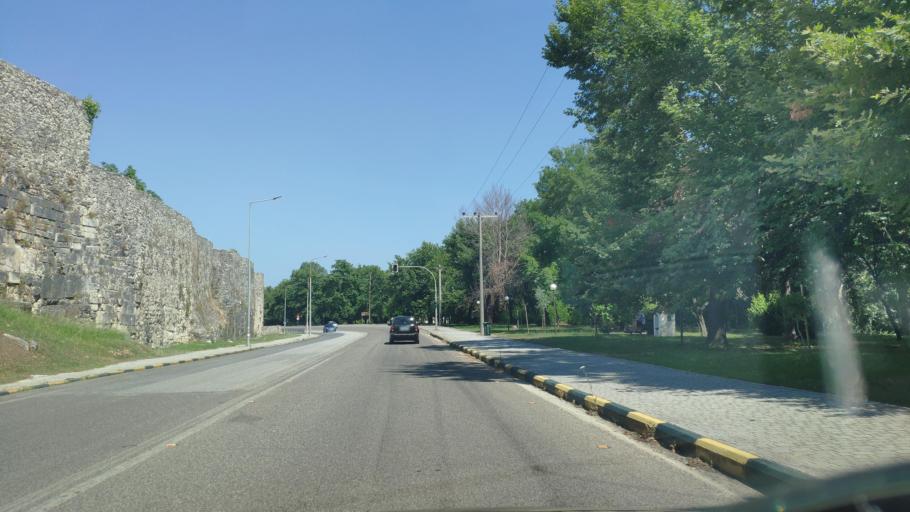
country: GR
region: Epirus
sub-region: Nomos Artas
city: Arta
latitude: 39.1659
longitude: 20.9893
